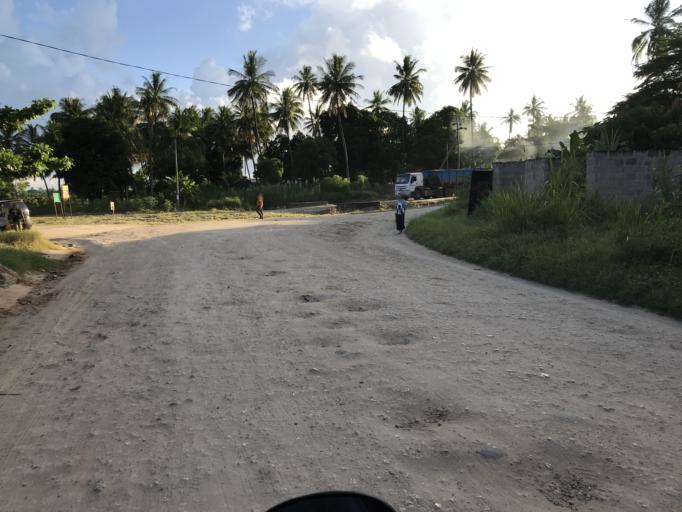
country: TZ
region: Dar es Salaam
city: Dar es Salaam
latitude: -6.8635
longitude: 39.3600
